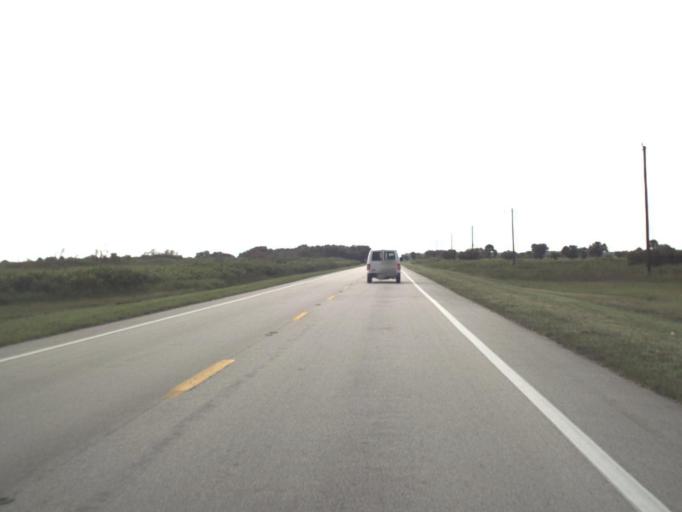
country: US
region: Florida
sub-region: Hendry County
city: Port LaBelle
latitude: 26.9144
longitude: -81.3248
